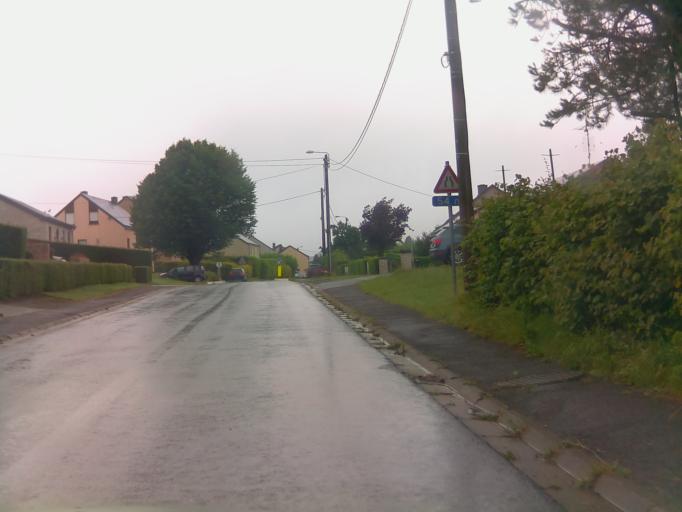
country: BE
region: Wallonia
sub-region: Province du Luxembourg
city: Saint-Leger
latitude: 49.6744
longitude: 5.6650
